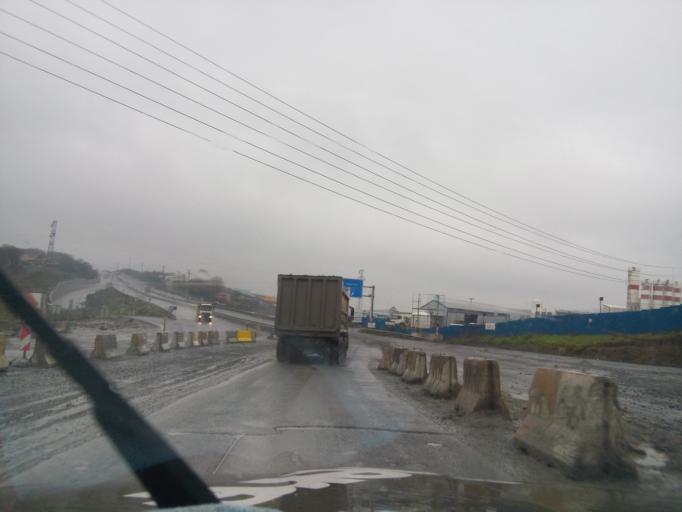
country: TR
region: Istanbul
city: Kemerburgaz
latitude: 41.2404
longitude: 28.8121
